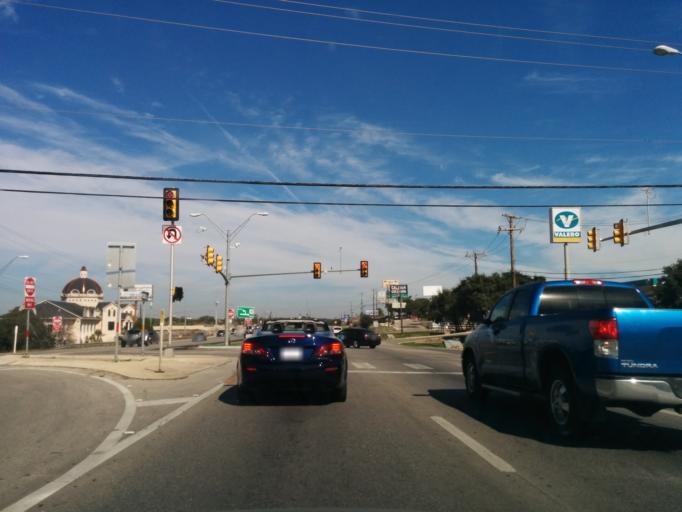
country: US
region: Texas
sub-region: Bexar County
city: Timberwood Park
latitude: 29.6606
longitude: -98.4501
